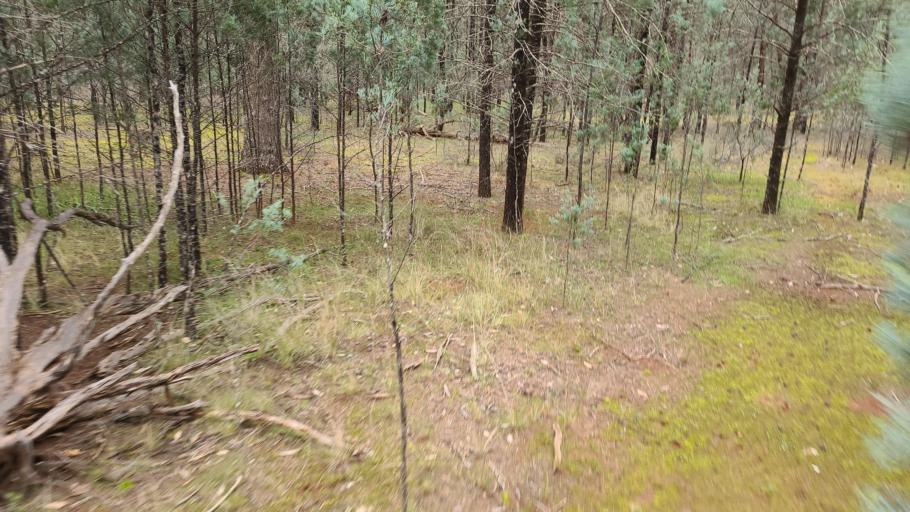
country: AU
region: New South Wales
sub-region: Coolamon
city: Coolamon
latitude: -34.8579
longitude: 146.9228
